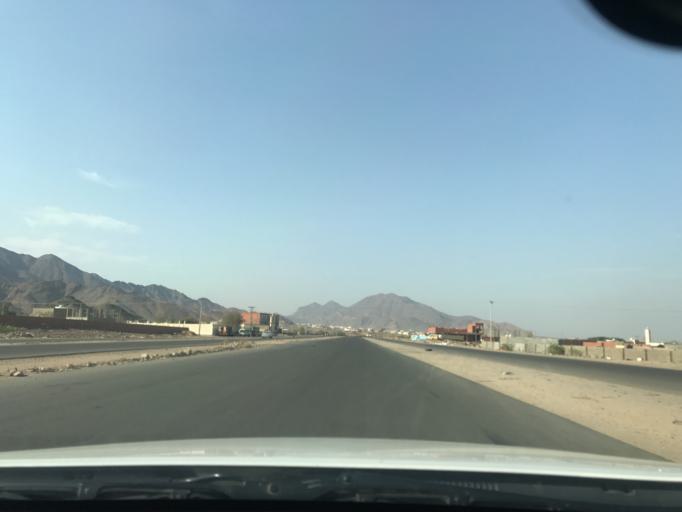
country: SA
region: Makkah
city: Al Jumum
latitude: 21.4454
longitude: 39.5190
